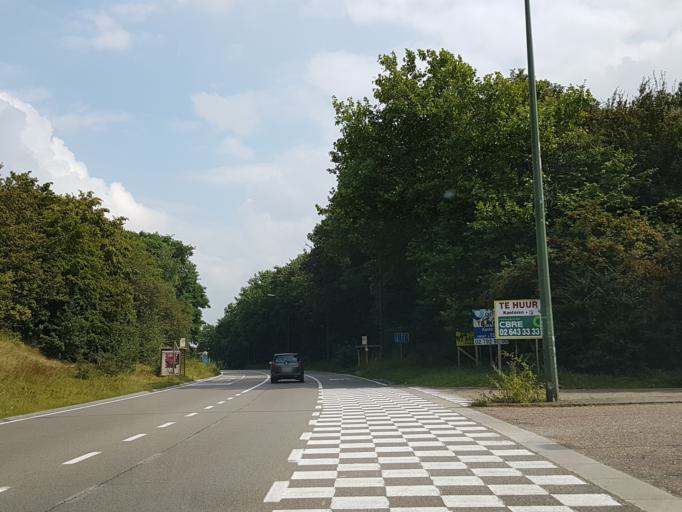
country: BE
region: Flanders
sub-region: Provincie Vlaams-Brabant
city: Zaventem
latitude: 50.8807
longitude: 4.4519
